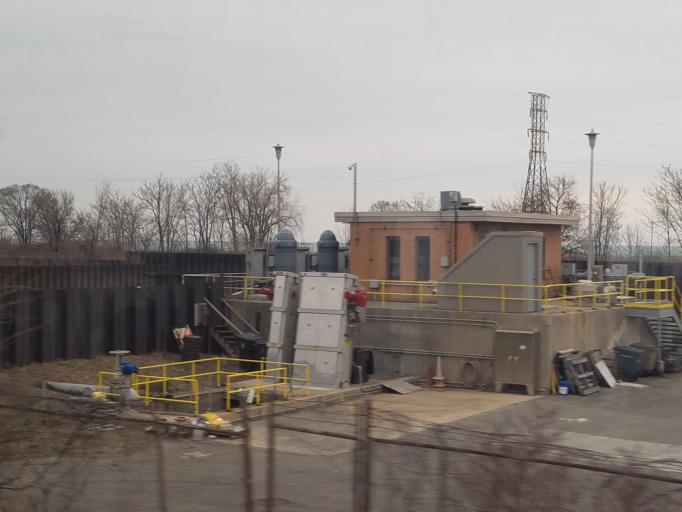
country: US
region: Indiana
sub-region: Lake County
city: Whiting
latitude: 41.6852
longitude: -87.4973
